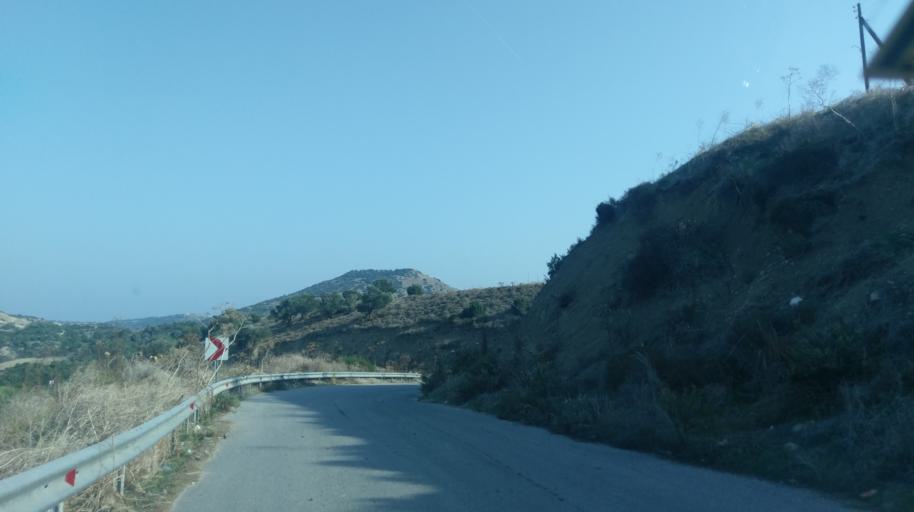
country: CY
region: Ammochostos
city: Rizokarpaso
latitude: 35.5132
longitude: 34.2762
